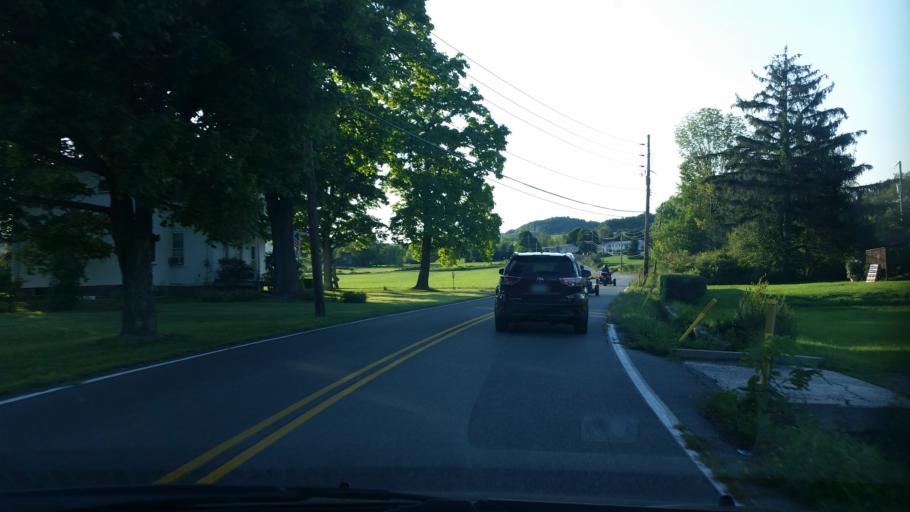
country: US
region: Pennsylvania
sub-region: Blair County
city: Greenwood
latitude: 40.5763
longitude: -78.3664
